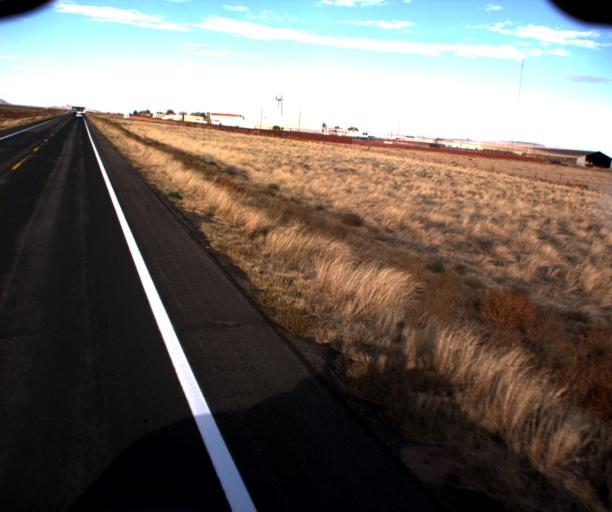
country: US
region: Arizona
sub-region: Apache County
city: Lukachukai
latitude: 36.9606
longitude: -109.3752
